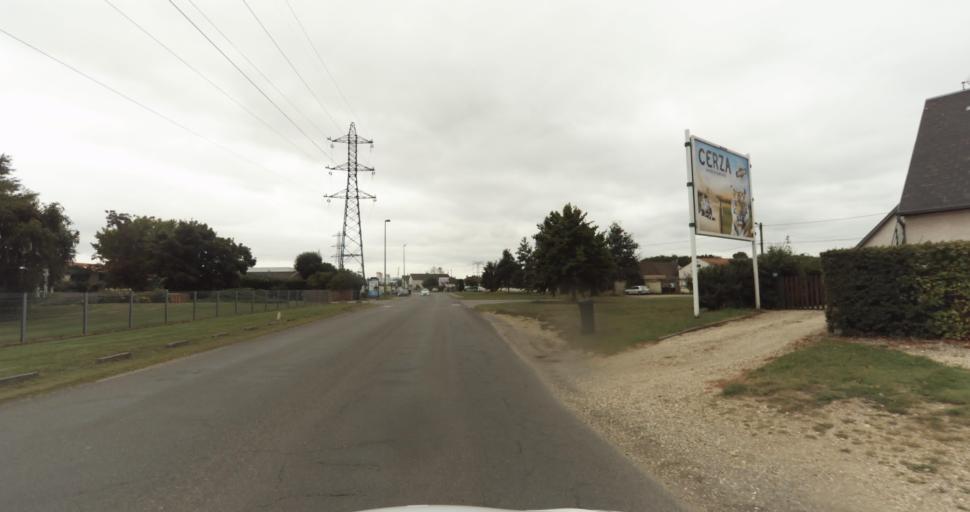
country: FR
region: Haute-Normandie
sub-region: Departement de l'Eure
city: Evreux
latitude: 49.0239
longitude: 1.1805
